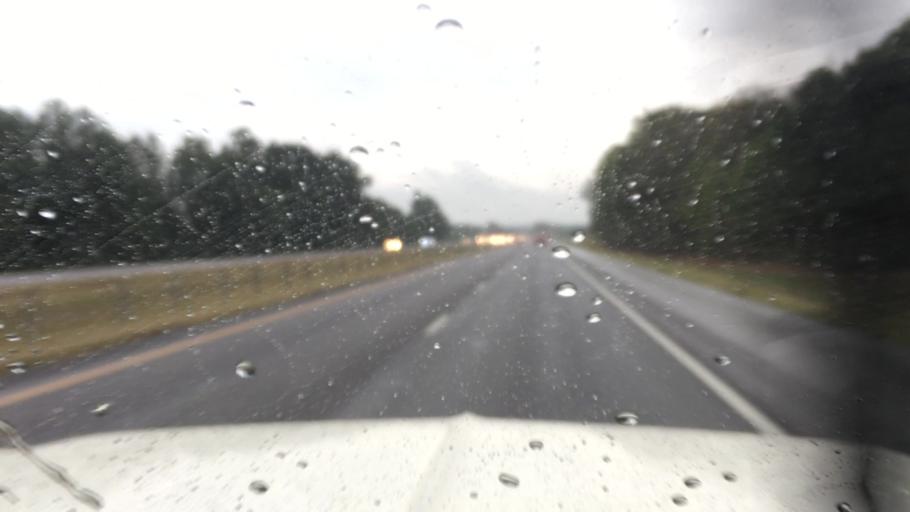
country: US
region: Alabama
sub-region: Morgan County
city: Hartselle
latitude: 34.4209
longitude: -86.8989
